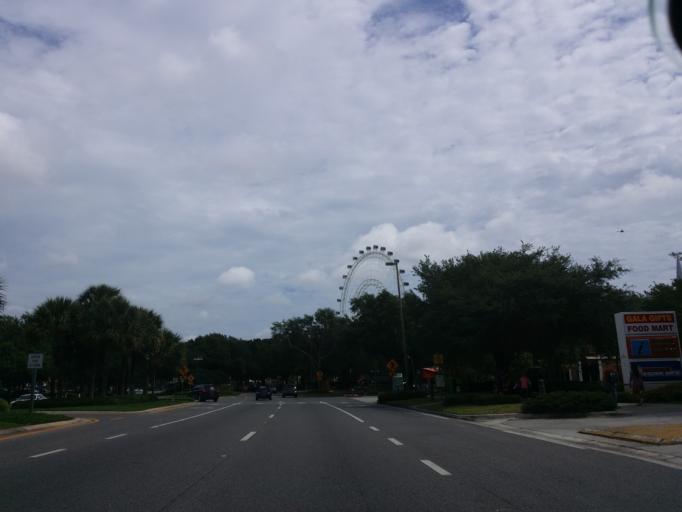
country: US
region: Florida
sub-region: Orange County
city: Doctor Phillips
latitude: 28.4393
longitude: -81.4711
